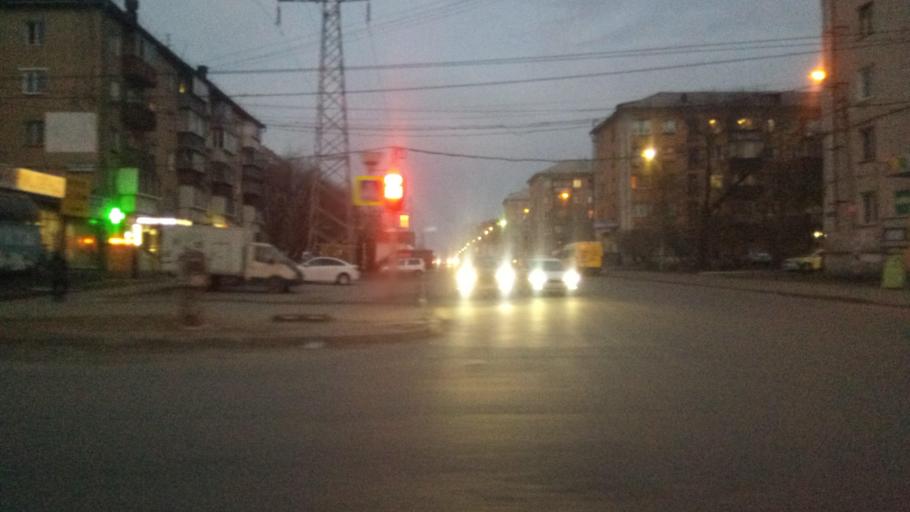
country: RU
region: Chelyabinsk
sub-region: Gorod Chelyabinsk
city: Chelyabinsk
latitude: 55.1702
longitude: 61.4624
